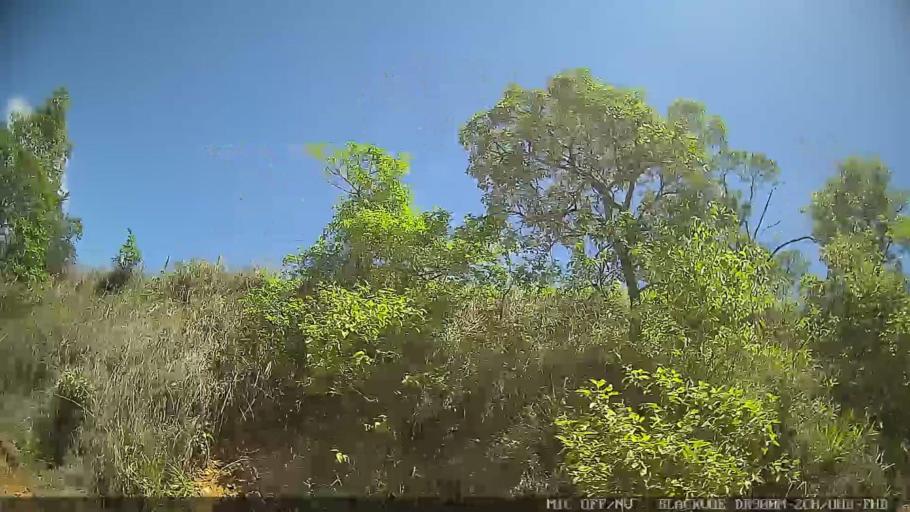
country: BR
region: Sao Paulo
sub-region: Pedreira
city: Pedreira
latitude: -22.7538
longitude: -46.9174
